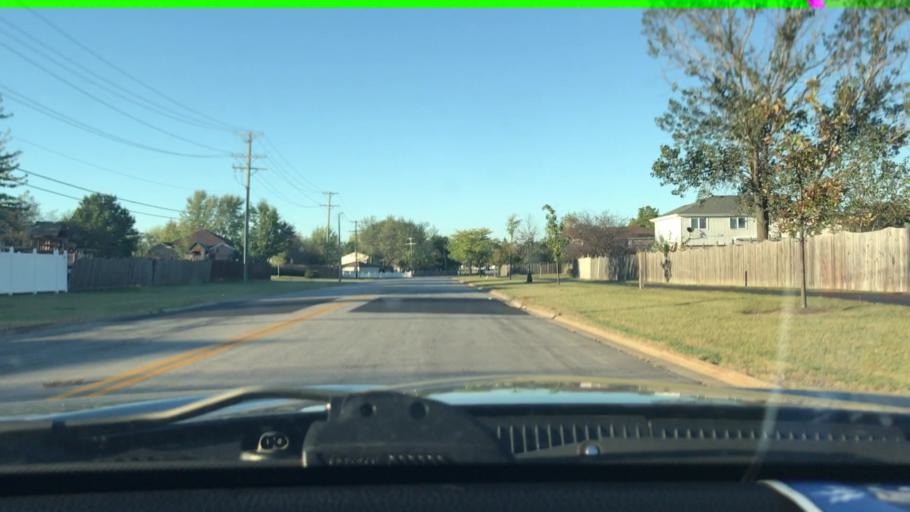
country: US
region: Illinois
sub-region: Will County
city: Frankfort Square
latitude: 41.5220
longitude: -87.8113
